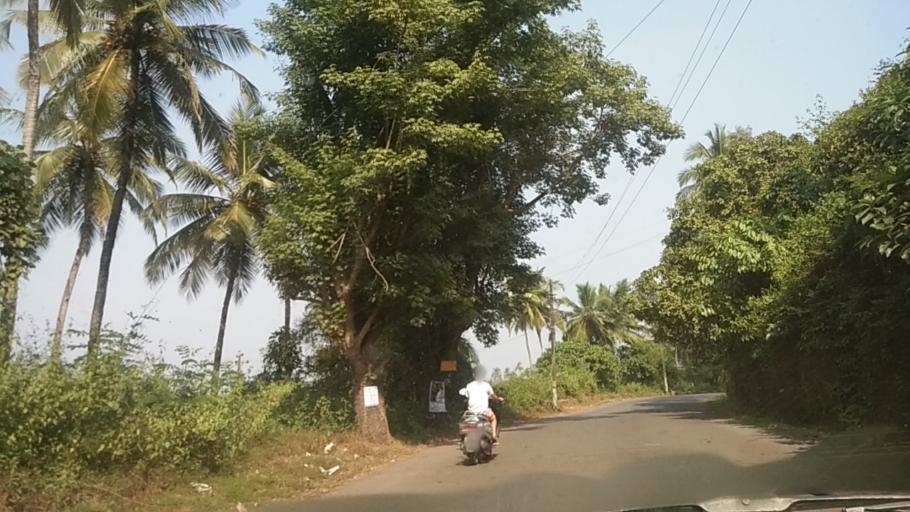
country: IN
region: Goa
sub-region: South Goa
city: Cavelossim
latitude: 15.1480
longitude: 73.9571
